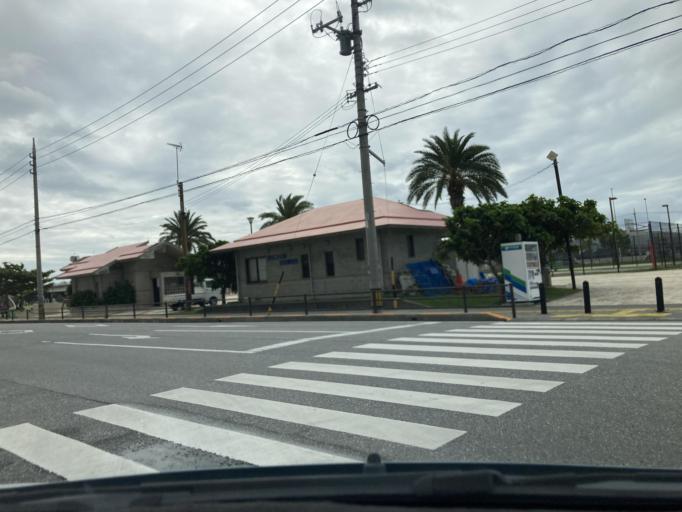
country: JP
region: Okinawa
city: Itoman
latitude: 26.1543
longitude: 127.6593
